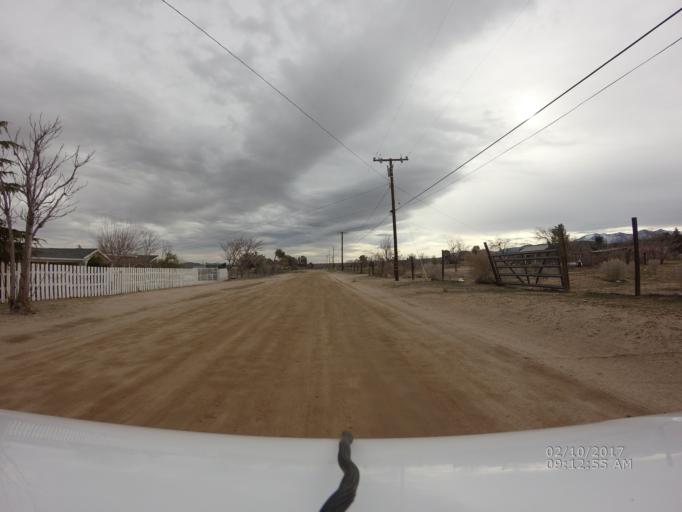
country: US
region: California
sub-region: Los Angeles County
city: Littlerock
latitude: 34.4918
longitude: -117.8937
